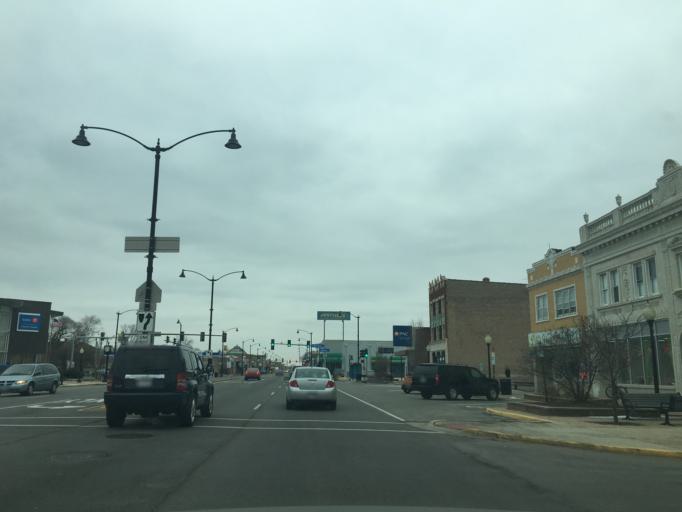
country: US
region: Illinois
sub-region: Cook County
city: Berwyn
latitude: 41.8508
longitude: -87.7896
